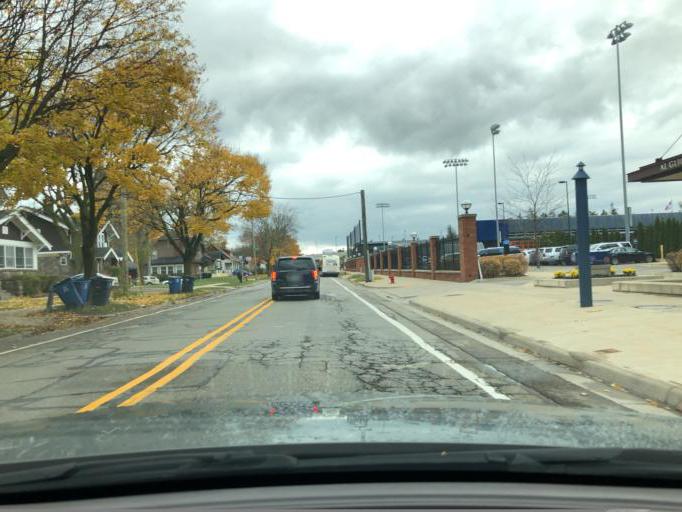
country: US
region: Michigan
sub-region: Washtenaw County
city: Ann Arbor
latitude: 42.2650
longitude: -83.7405
